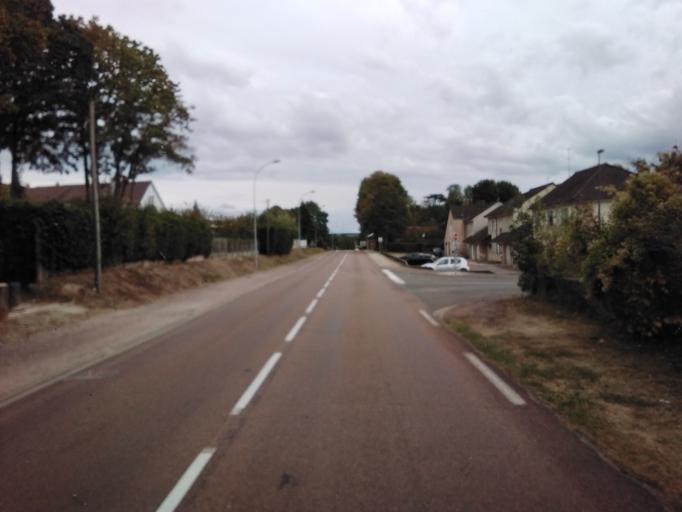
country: FR
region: Champagne-Ardenne
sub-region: Departement de l'Aube
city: Bar-sur-Seine
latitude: 48.1206
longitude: 4.3840
